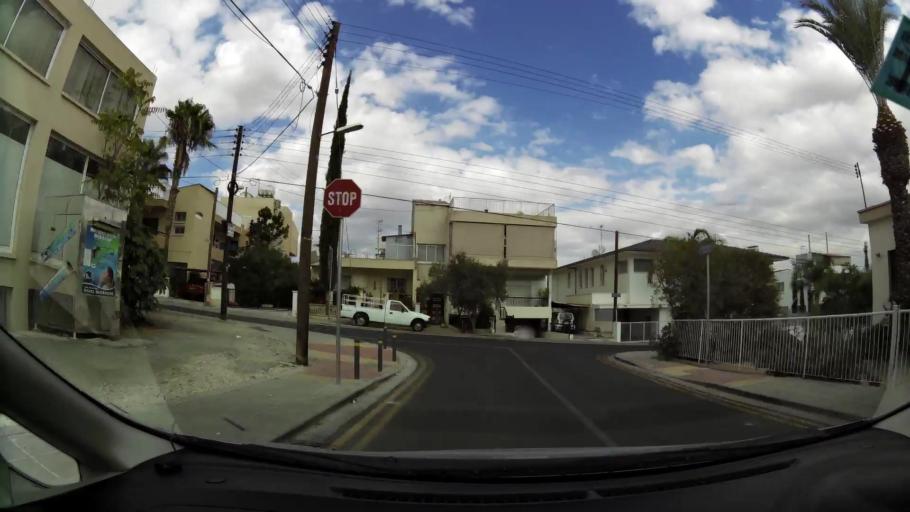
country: CY
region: Lefkosia
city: Nicosia
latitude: 35.1776
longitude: 33.3879
